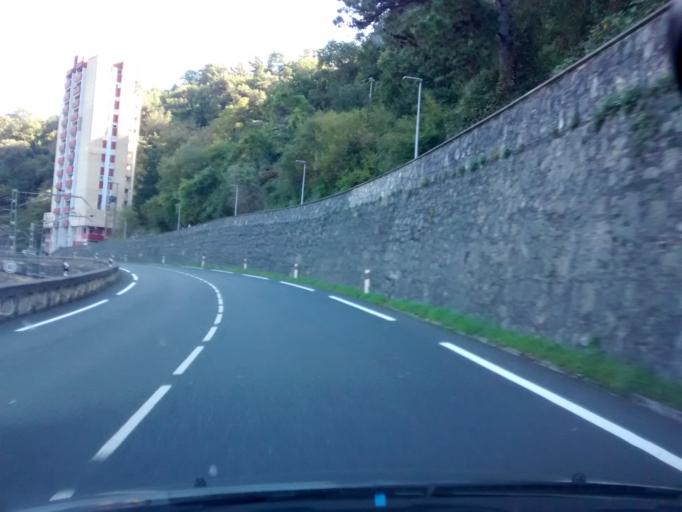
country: ES
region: Basque Country
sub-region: Provincia de Guipuzcoa
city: Deba
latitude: 43.2881
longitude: -2.3594
